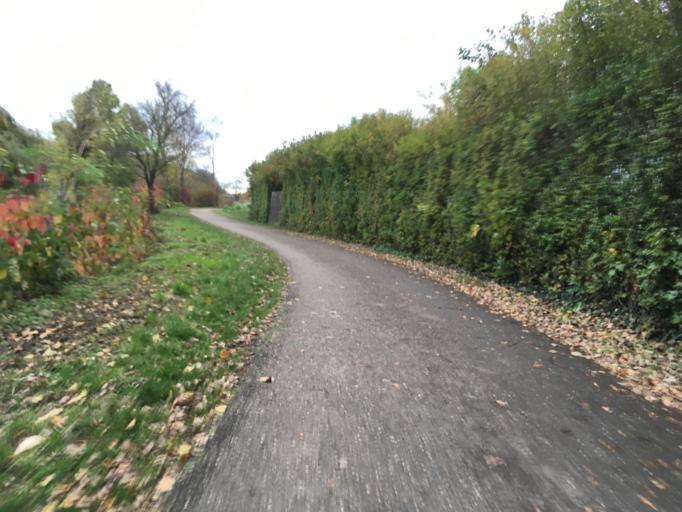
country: DE
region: Baden-Wuerttemberg
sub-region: Freiburg Region
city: Botzingen
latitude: 48.0809
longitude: 7.7381
